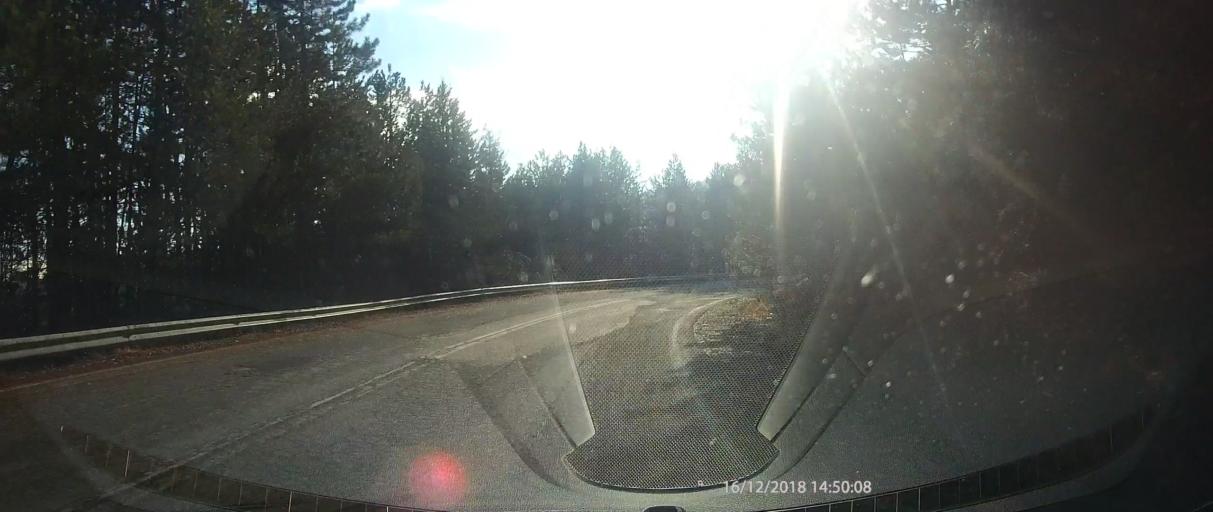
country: GR
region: West Macedonia
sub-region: Nomos Kastorias
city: Nestorio
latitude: 40.2076
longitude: 21.0829
